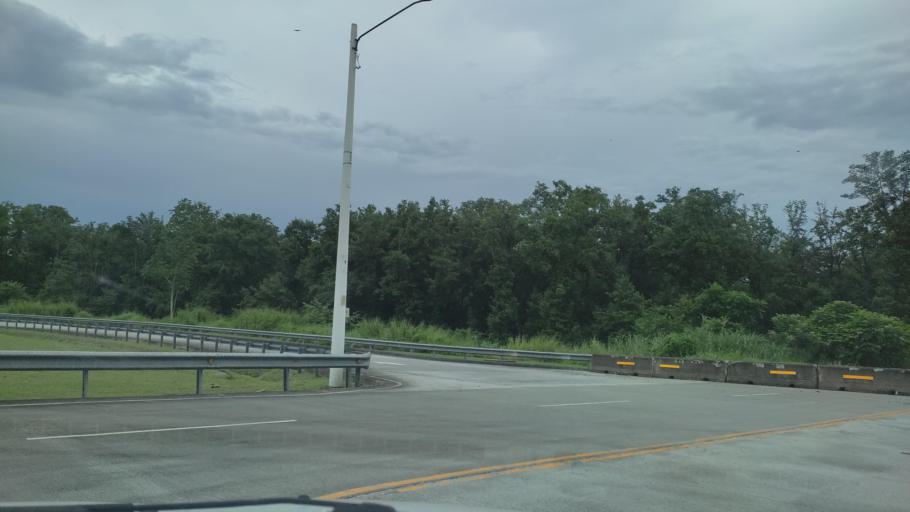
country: PA
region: Panama
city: San Miguelito
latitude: 9.0325
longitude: -79.4400
